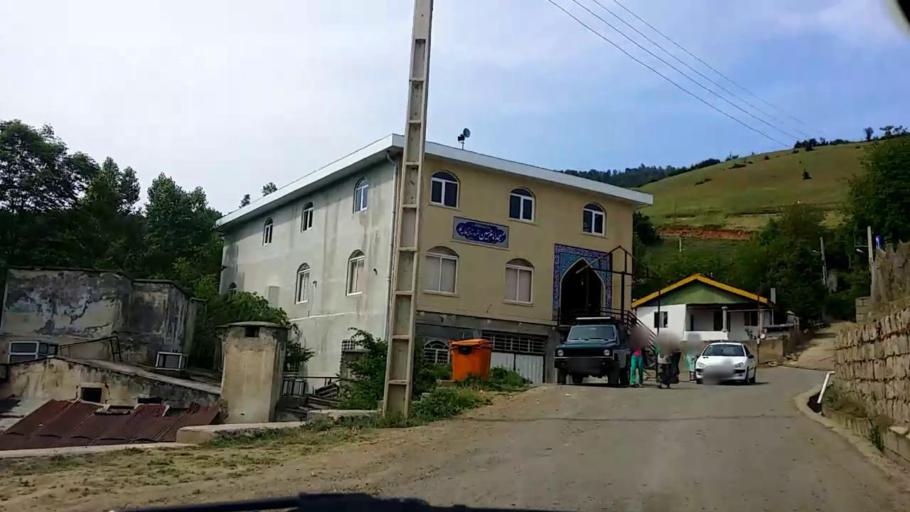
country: IR
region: Mazandaran
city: `Abbasabad
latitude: 36.5543
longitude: 51.1808
